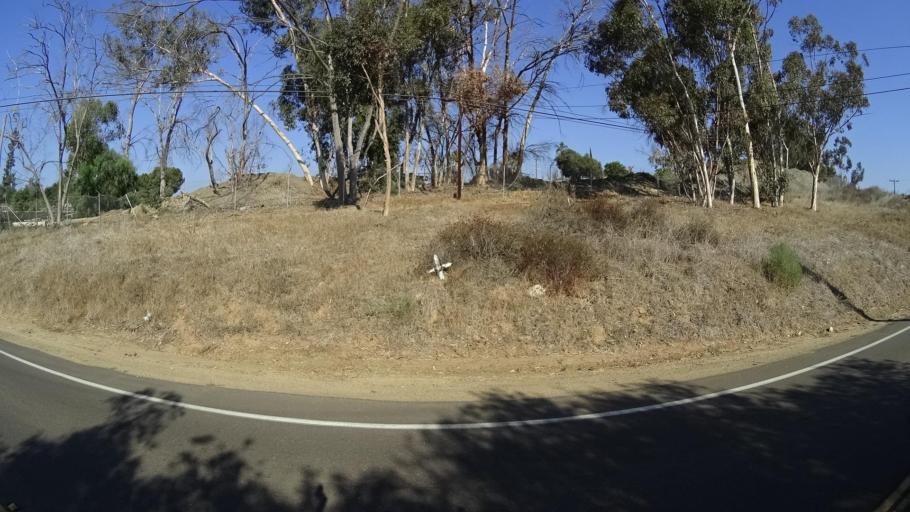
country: US
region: California
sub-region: San Diego County
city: Fallbrook
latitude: 33.3411
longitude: -117.2447
